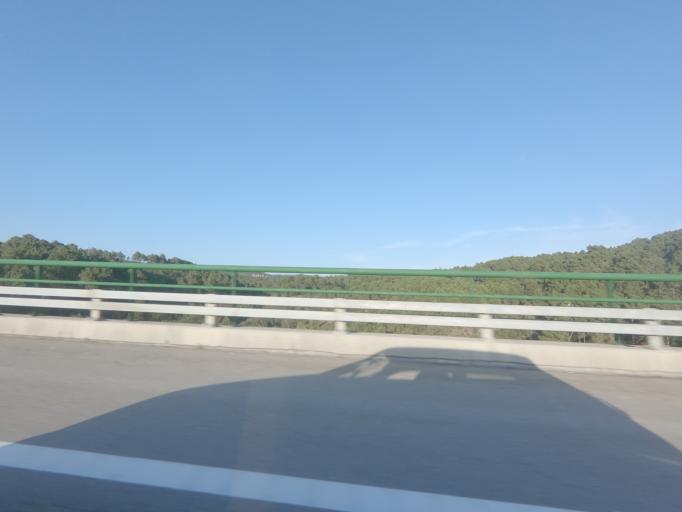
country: PT
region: Vila Real
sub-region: Vila Real
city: Vila Real
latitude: 41.3096
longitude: -7.6859
